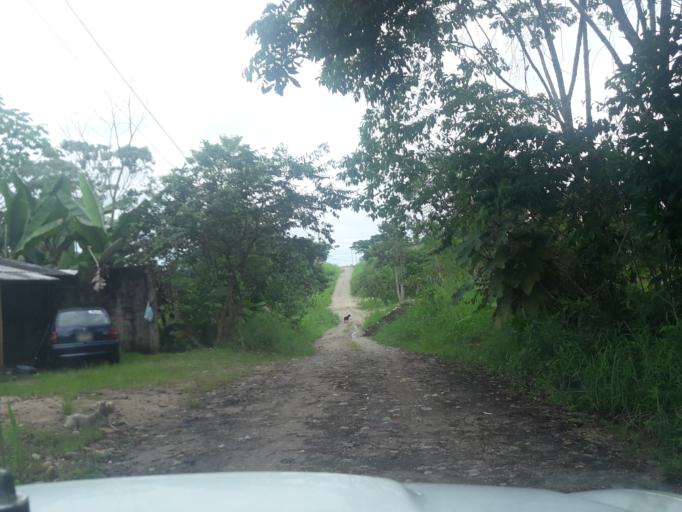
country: EC
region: Napo
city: Archidona
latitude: -0.9446
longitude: -77.8163
